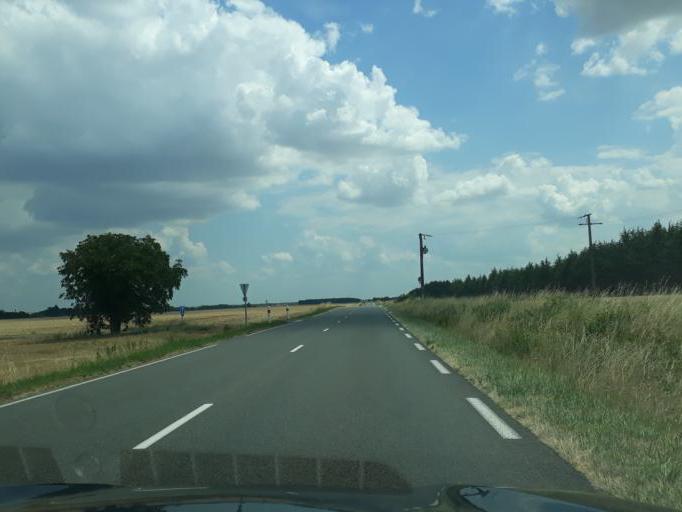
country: FR
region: Centre
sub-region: Departement du Cher
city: Avord
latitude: 47.0386
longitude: 2.5922
